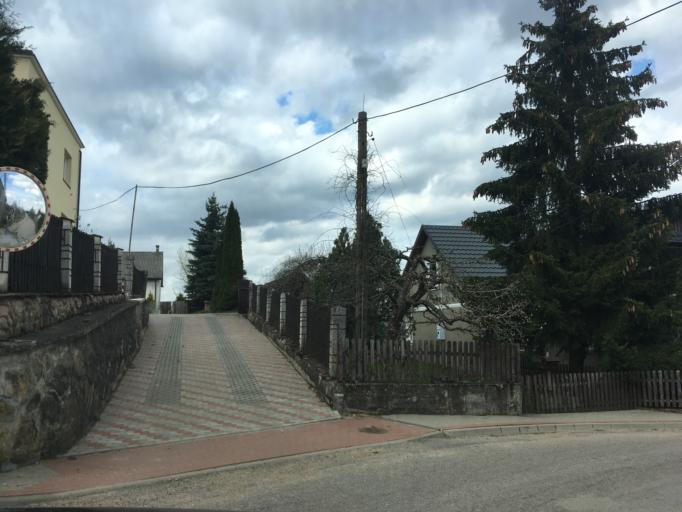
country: PL
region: Podlasie
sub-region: Suwalki
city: Suwalki
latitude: 54.3681
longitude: 22.8695
